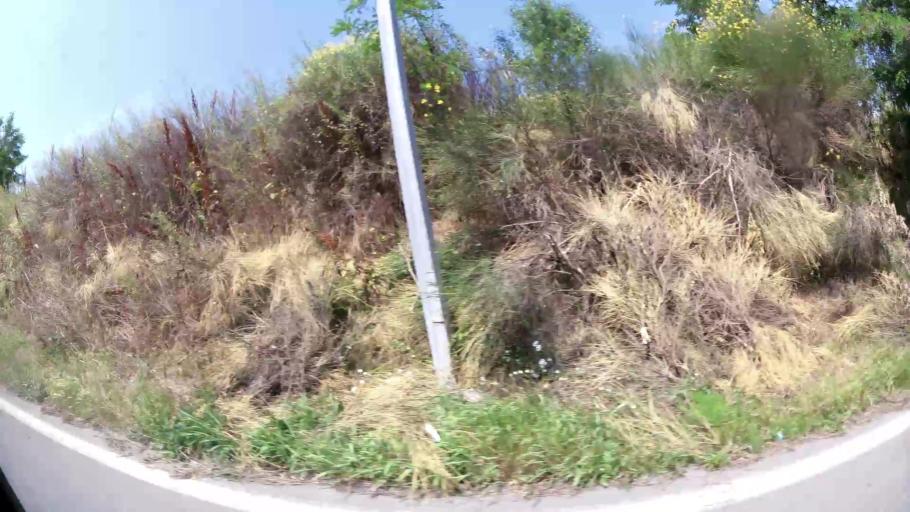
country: GR
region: West Macedonia
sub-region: Nomos Kozanis
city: Koila
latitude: 40.3200
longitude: 21.7880
